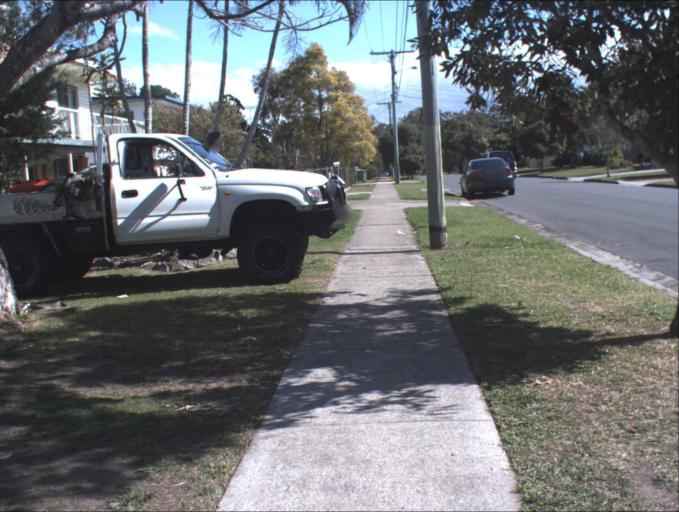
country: AU
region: Queensland
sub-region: Logan
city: Waterford West
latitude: -27.6838
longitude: 153.1089
